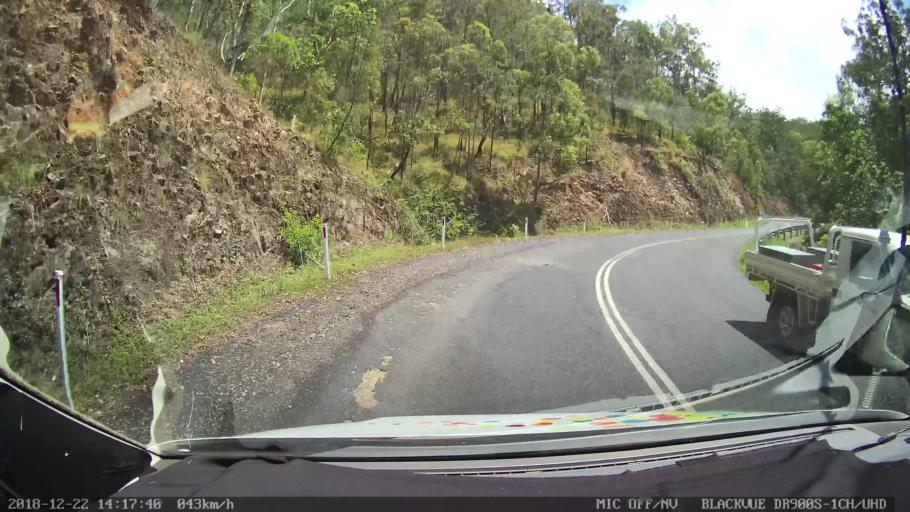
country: AU
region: New South Wales
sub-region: Clarence Valley
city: Coutts Crossing
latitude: -30.0097
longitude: 152.6681
